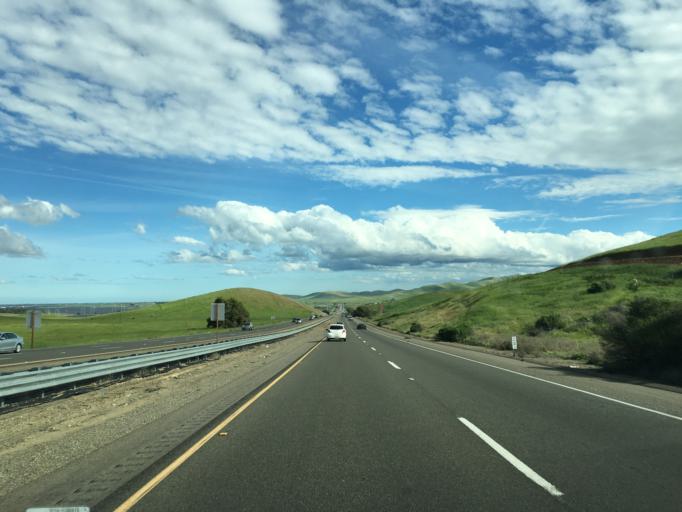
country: US
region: California
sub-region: Merced County
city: Gustine
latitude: 37.0809
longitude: -121.0919
